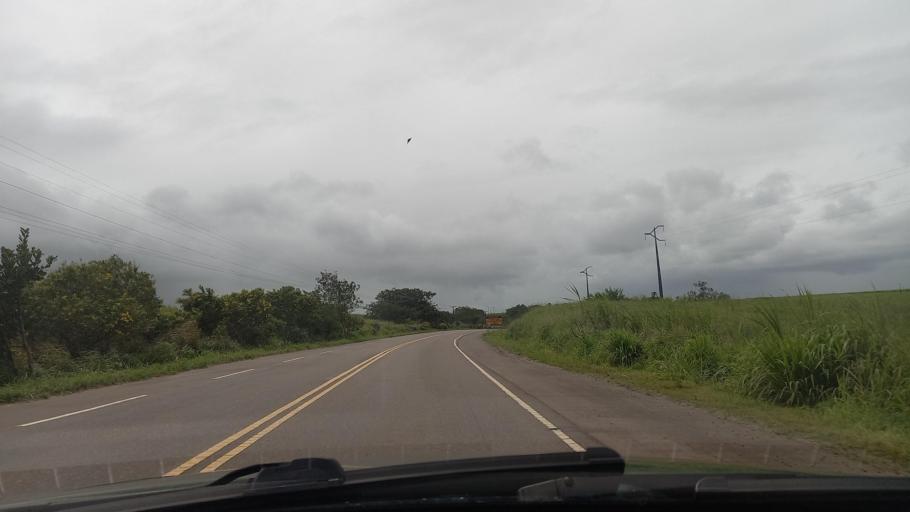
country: BR
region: Alagoas
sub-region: Sao Miguel Dos Campos
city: Sao Miguel dos Campos
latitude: -9.8057
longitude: -36.2074
